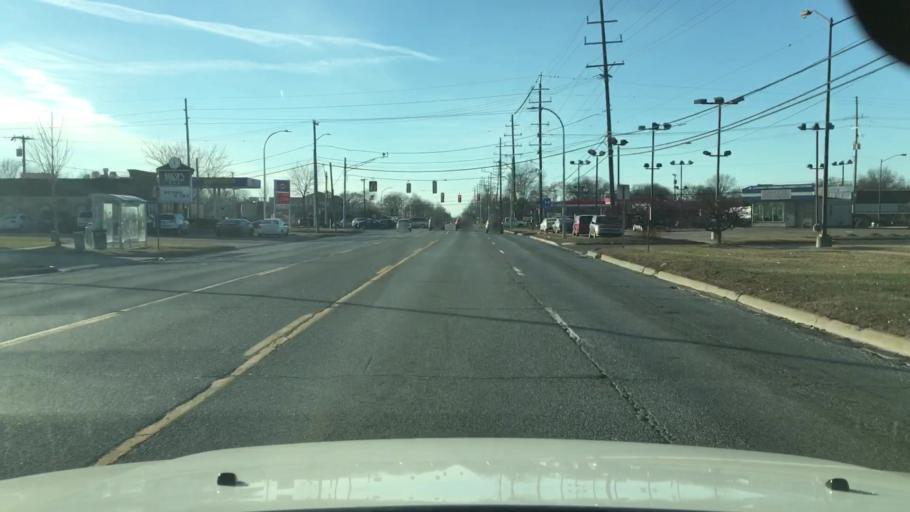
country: US
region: Michigan
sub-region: Oakland County
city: Madison Heights
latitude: 42.5053
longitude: -83.0840
